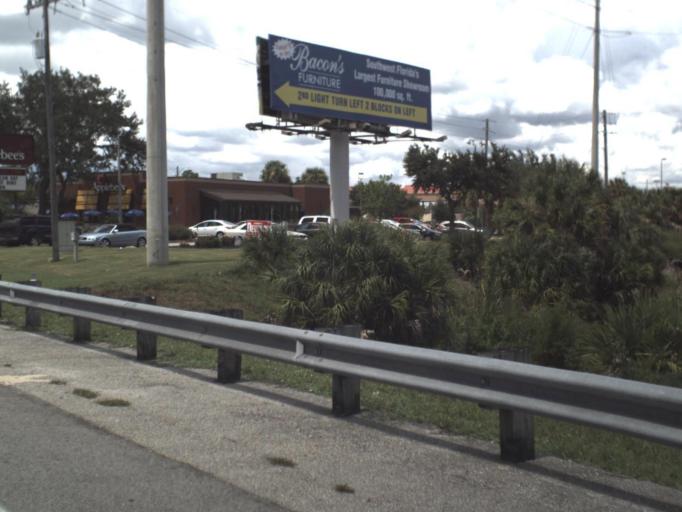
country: US
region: Florida
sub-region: Charlotte County
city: Port Charlotte
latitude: 27.0099
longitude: -82.1393
